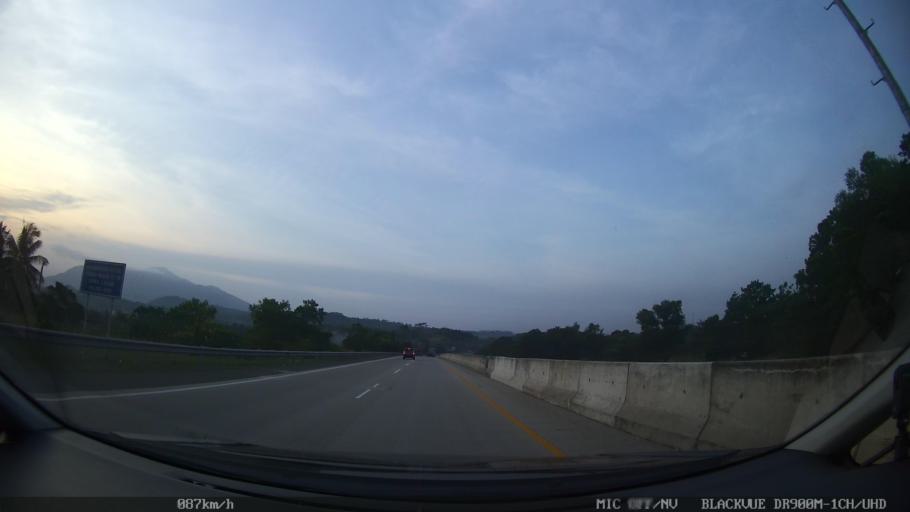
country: ID
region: Lampung
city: Penengahan
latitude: -5.8510
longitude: 105.7283
